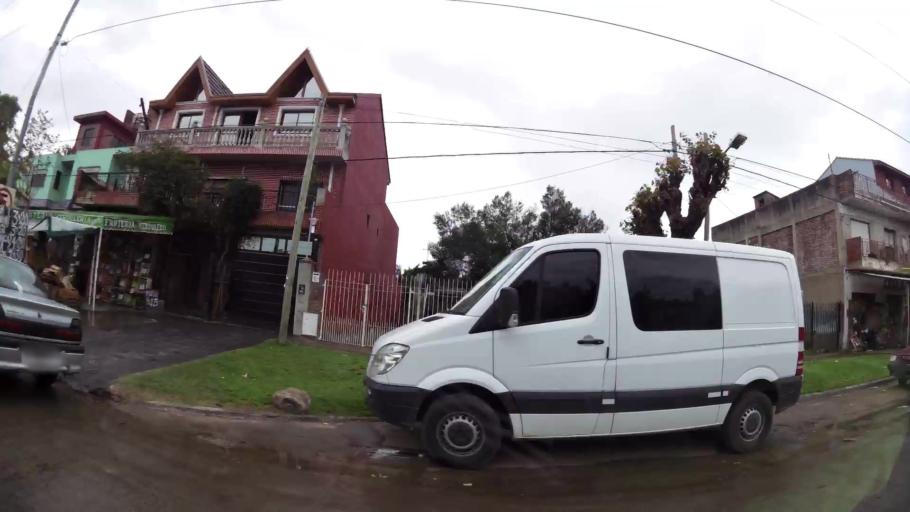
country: AR
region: Buenos Aires
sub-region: Partido de Quilmes
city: Quilmes
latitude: -34.7581
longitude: -58.2374
